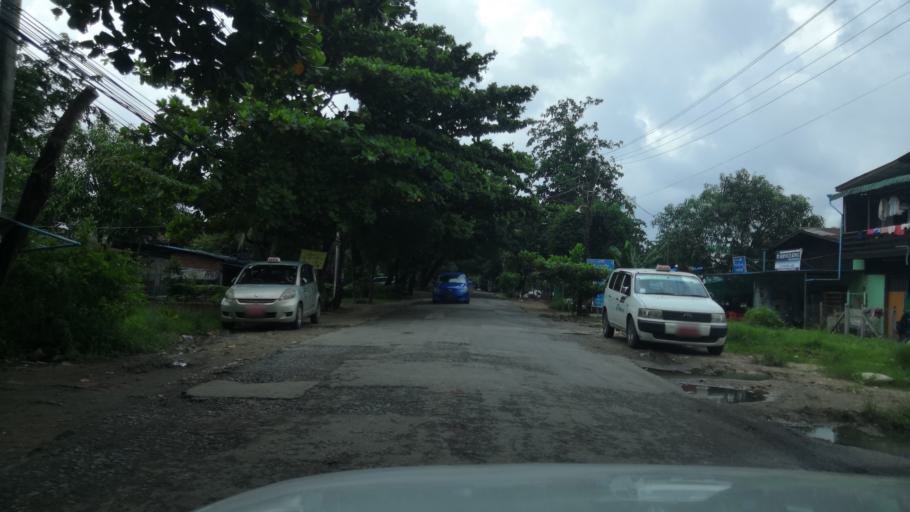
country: MM
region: Yangon
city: Yangon
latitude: 16.8882
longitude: 96.1756
